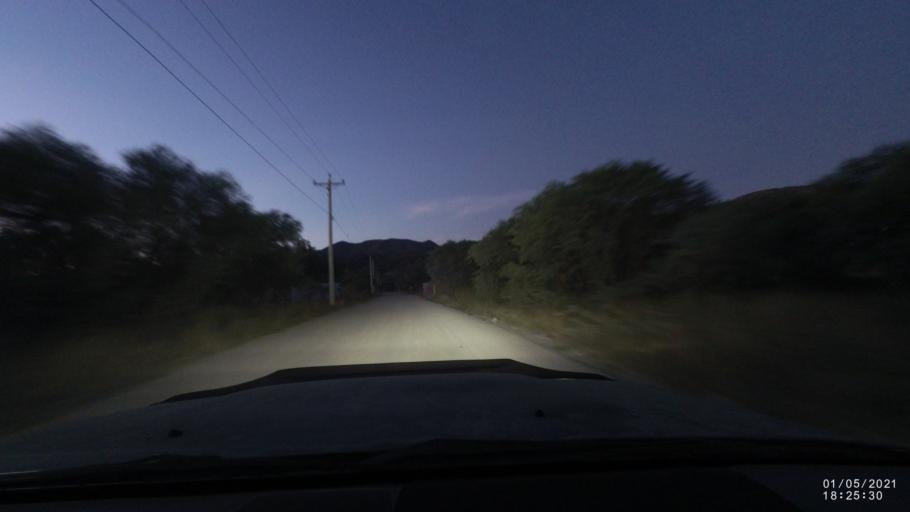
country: BO
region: Cochabamba
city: Capinota
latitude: -17.6548
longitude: -66.2420
